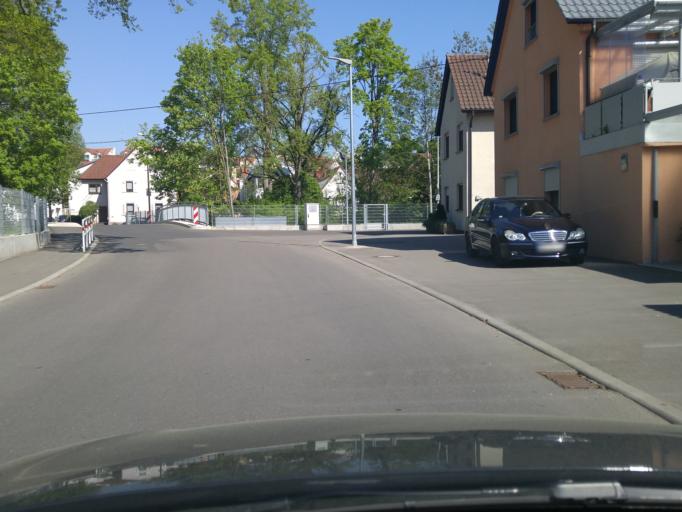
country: DE
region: Baden-Wuerttemberg
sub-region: Regierungsbezirk Stuttgart
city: Leingarten
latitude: 49.1472
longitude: 9.1049
